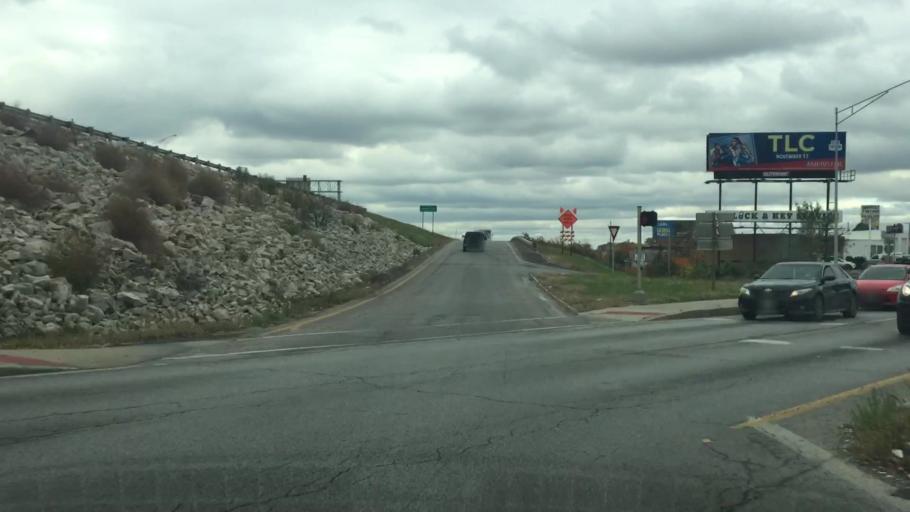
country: US
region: Missouri
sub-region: Jackson County
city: Raytown
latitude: 39.0476
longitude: -94.4439
